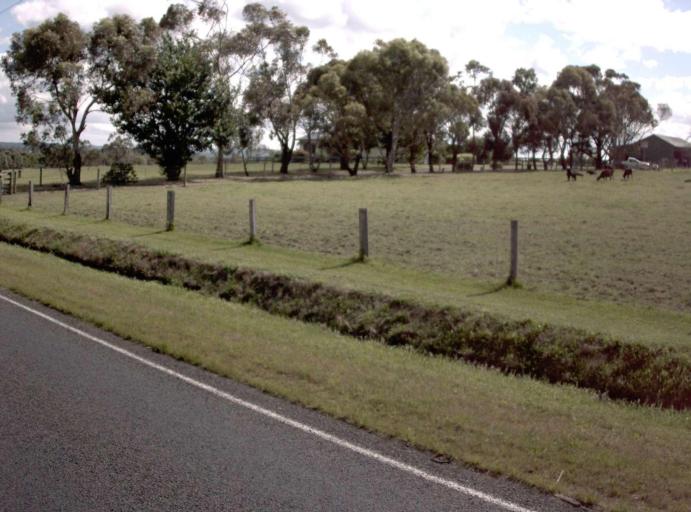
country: AU
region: Victoria
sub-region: Latrobe
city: Morwell
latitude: -38.2859
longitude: 146.4305
